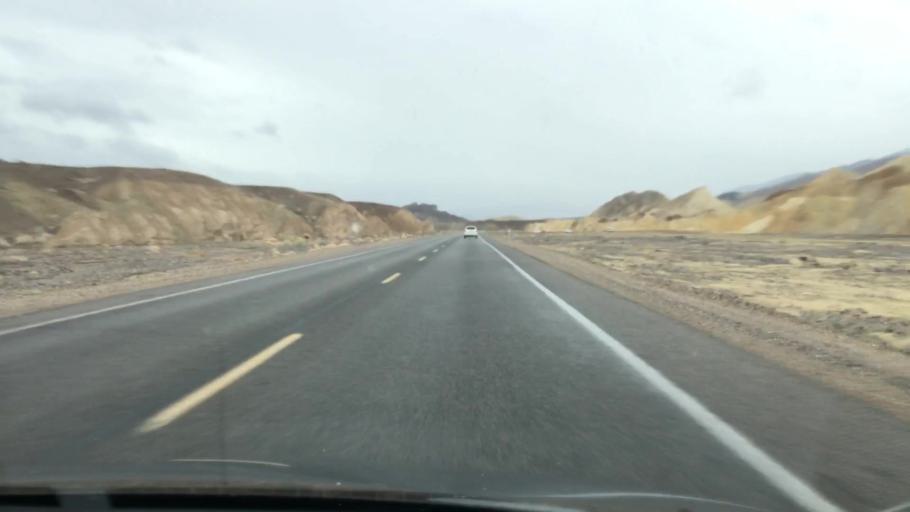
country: US
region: Nevada
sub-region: Nye County
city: Beatty
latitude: 36.4111
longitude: -116.7984
